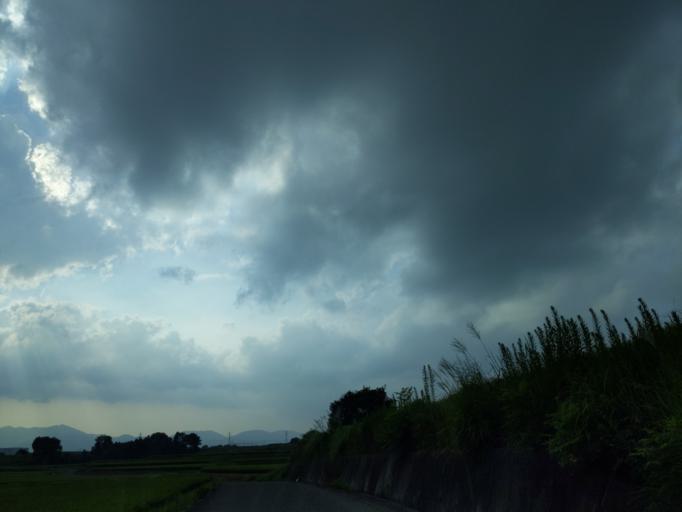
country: JP
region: Fukushima
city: Koriyama
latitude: 37.4372
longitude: 140.3667
